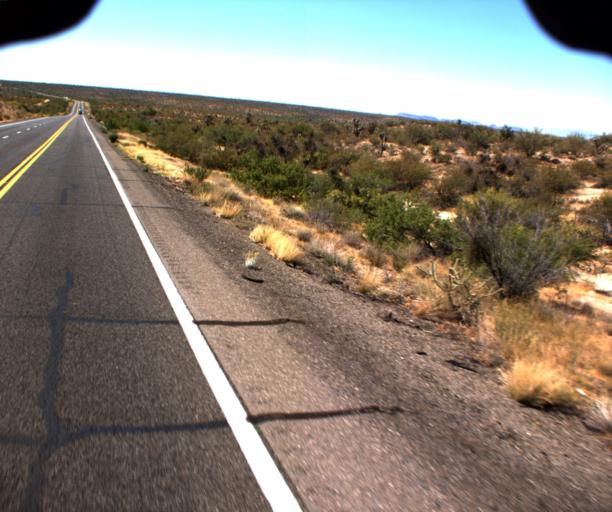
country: US
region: Arizona
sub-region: Yavapai County
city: Congress
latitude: 34.2161
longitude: -113.0674
